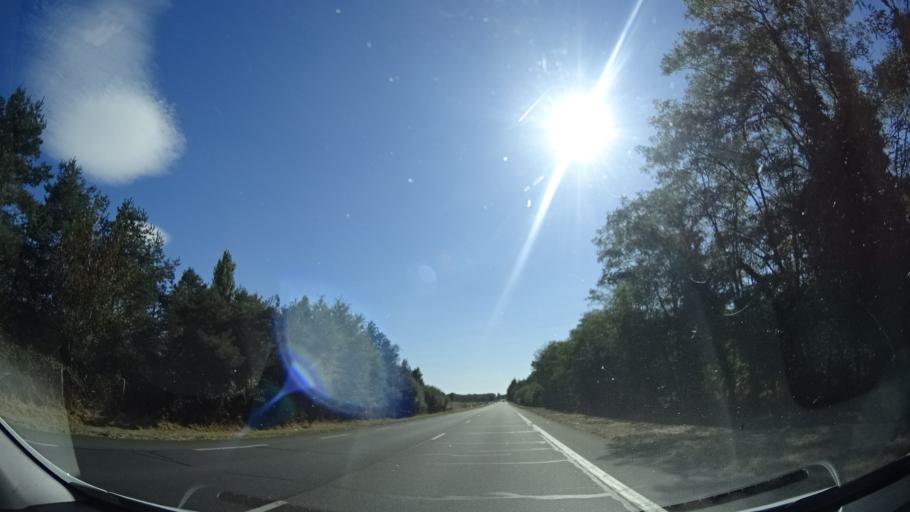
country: FR
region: Centre
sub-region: Departement du Loiret
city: Vitry-aux-Loges
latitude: 47.8995
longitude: 2.2830
